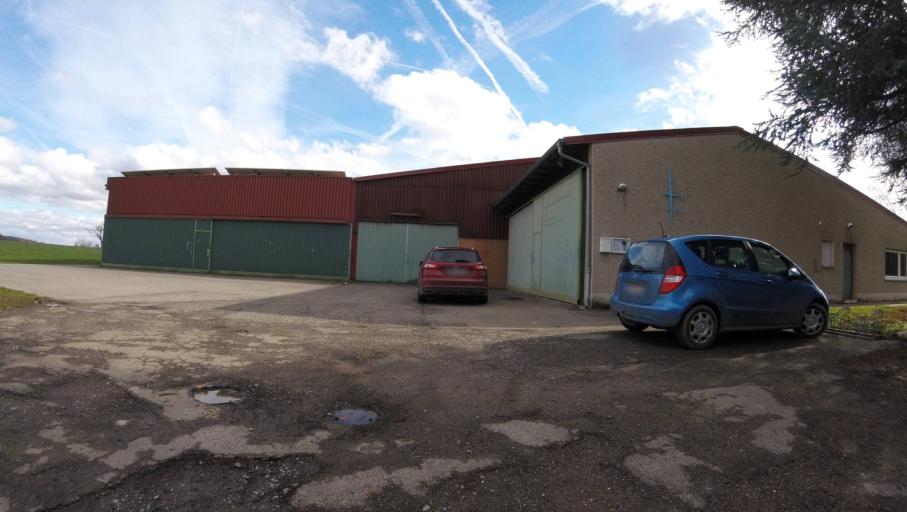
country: DE
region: Baden-Wuerttemberg
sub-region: Regierungsbezirk Stuttgart
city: Oberstenfeld
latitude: 49.0106
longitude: 9.3542
